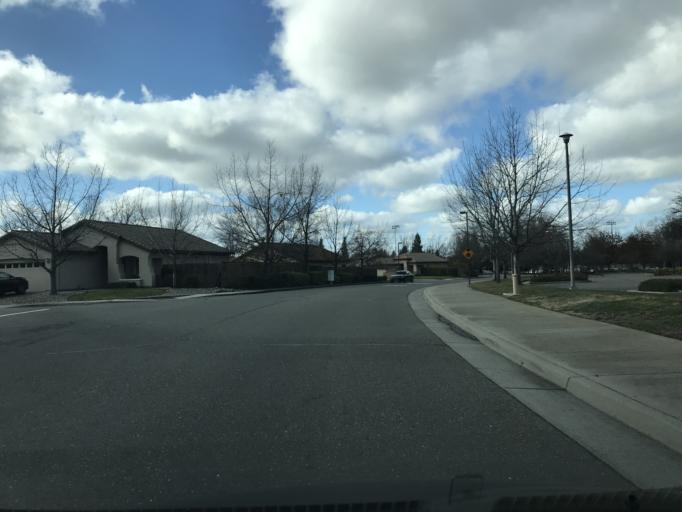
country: US
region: California
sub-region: Sacramento County
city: Folsom
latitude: 38.6529
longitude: -121.1311
